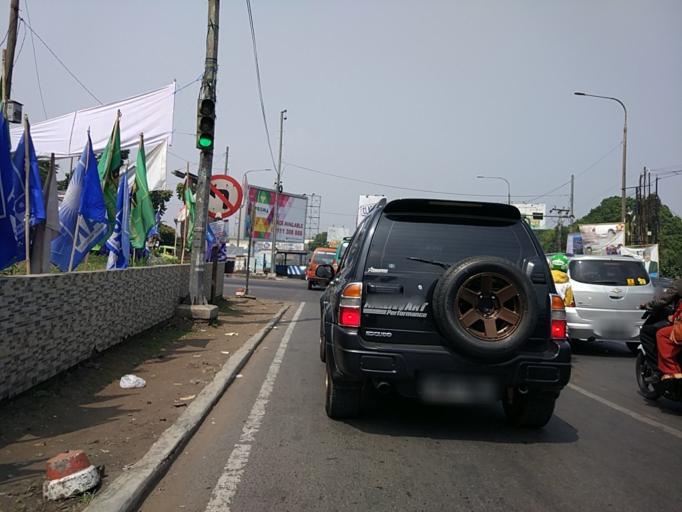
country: ID
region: West Java
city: Padalarang
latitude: -6.8518
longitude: 107.4975
